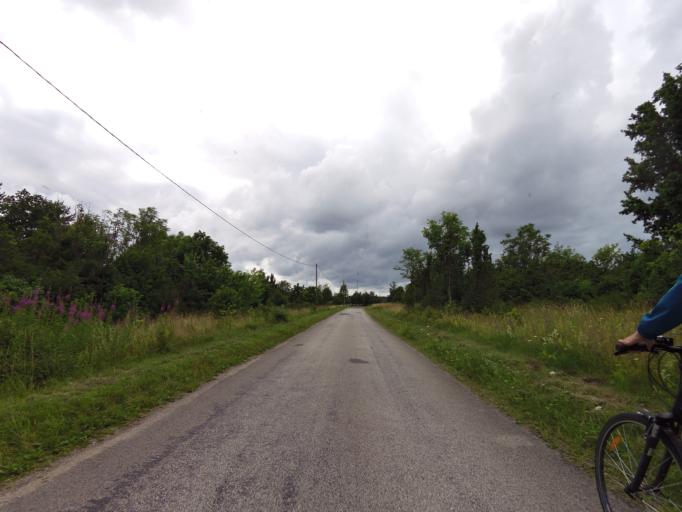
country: EE
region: Laeaene
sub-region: Vormsi vald
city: Hullo
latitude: 58.9857
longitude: 23.2471
